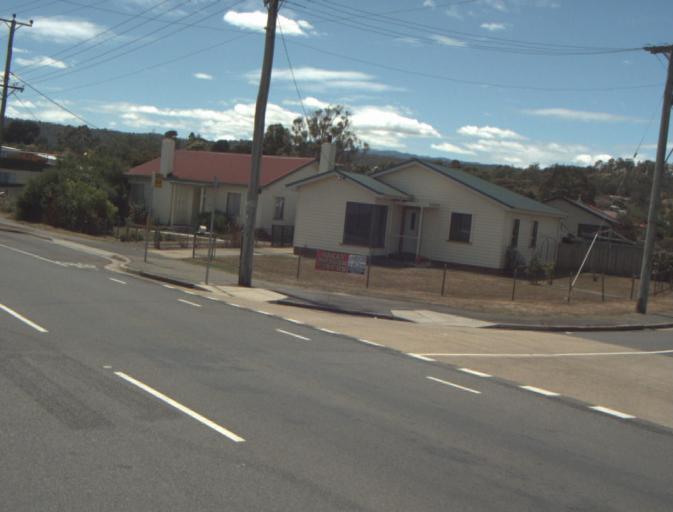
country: AU
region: Tasmania
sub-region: Launceston
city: Mayfield
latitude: -41.3830
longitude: 147.1284
